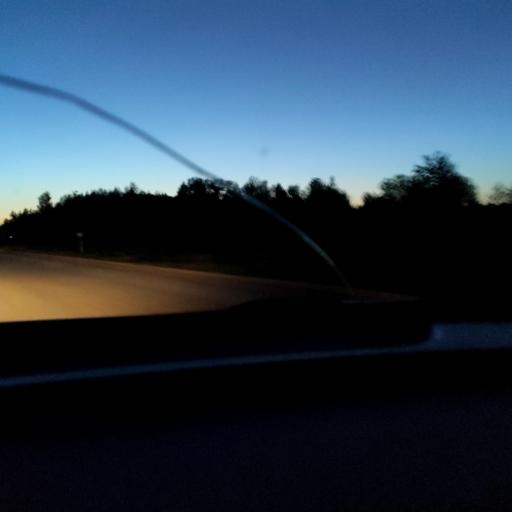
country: RU
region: Tatarstan
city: Osinovo
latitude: 55.8608
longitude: 48.9046
